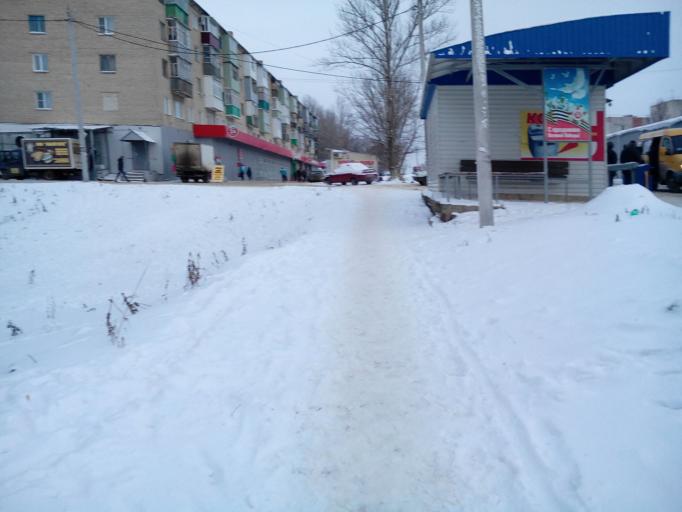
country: RU
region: Tula
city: Yefremov
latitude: 53.1497
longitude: 38.0759
